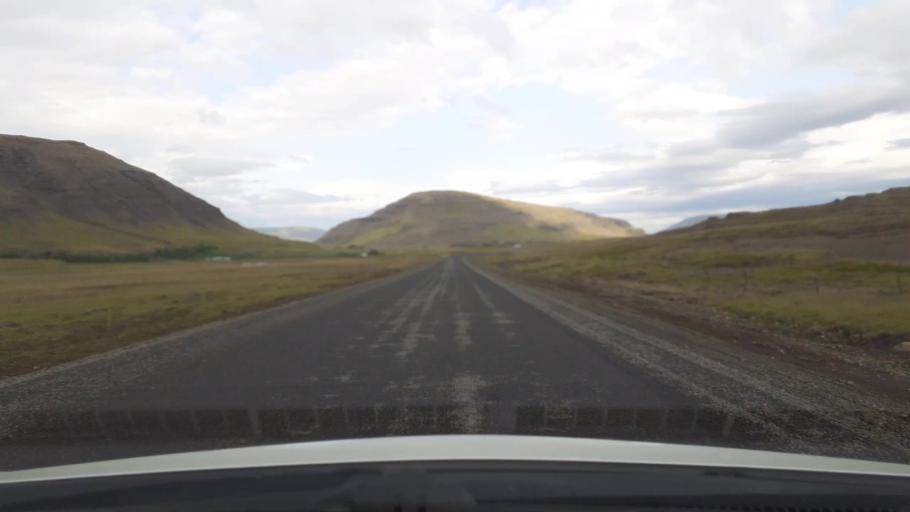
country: IS
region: Capital Region
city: Mosfellsbaer
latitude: 64.2992
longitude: -21.4762
